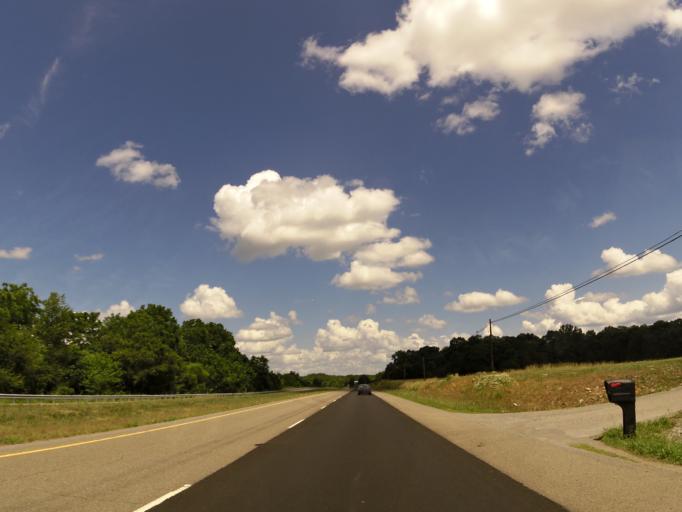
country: US
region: Virginia
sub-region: Lee County
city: Jonesville
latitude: 36.6728
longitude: -83.1767
